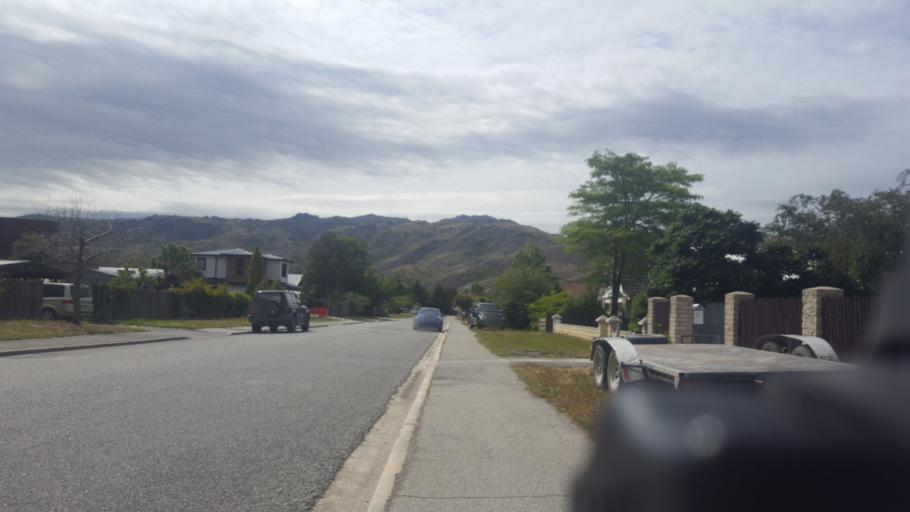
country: NZ
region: Otago
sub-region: Queenstown-Lakes District
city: Wanaka
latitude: -45.0417
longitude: 169.2002
